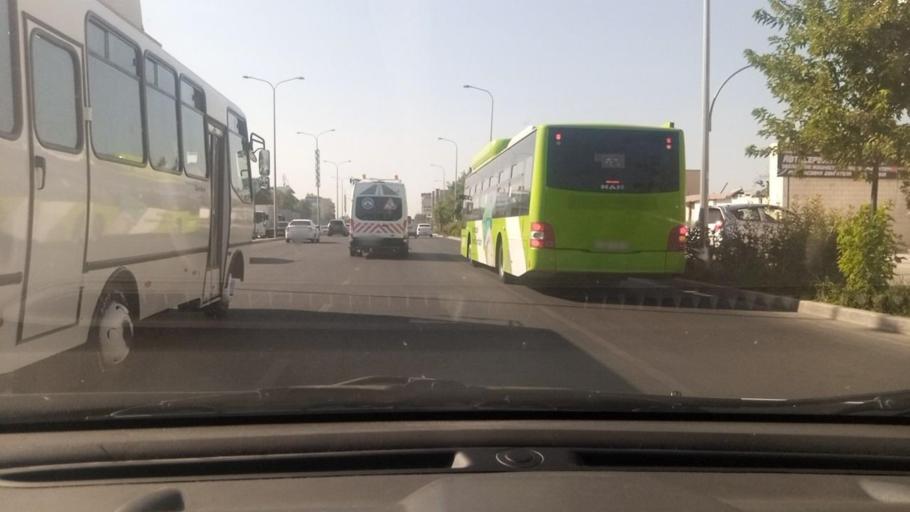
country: UZ
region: Toshkent Shahri
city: Bektemir
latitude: 41.2555
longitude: 69.3206
